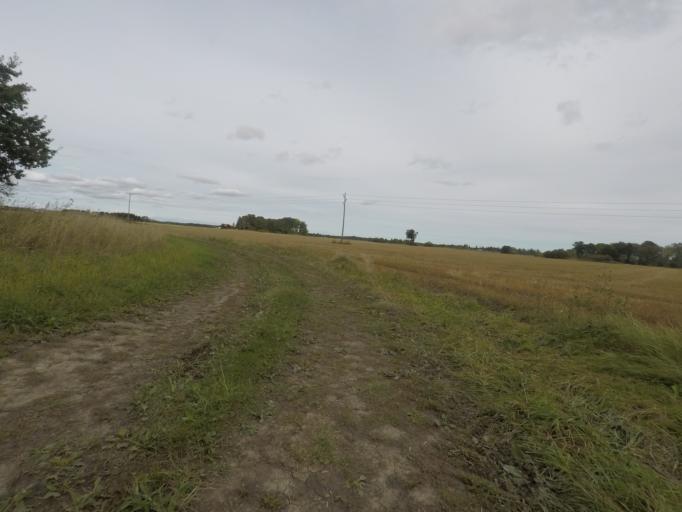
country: SE
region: Vaestmanland
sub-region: Kungsors Kommun
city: Kungsoer
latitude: 59.4555
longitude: 16.0501
